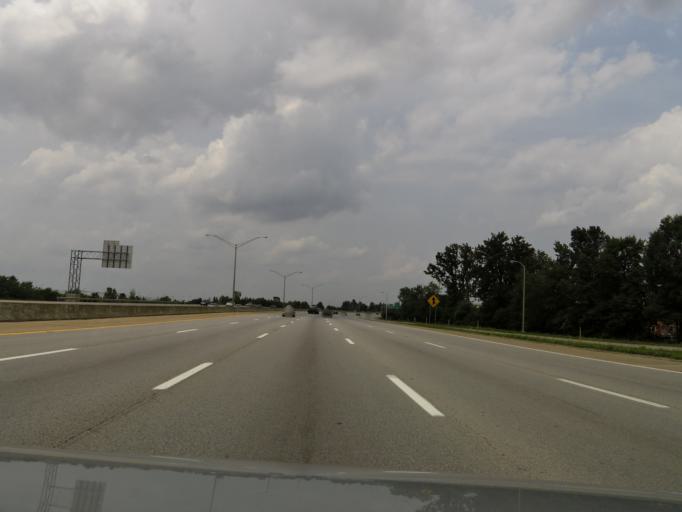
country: US
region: Kentucky
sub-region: Jefferson County
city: Heritage Creek
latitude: 38.1592
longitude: -85.7193
